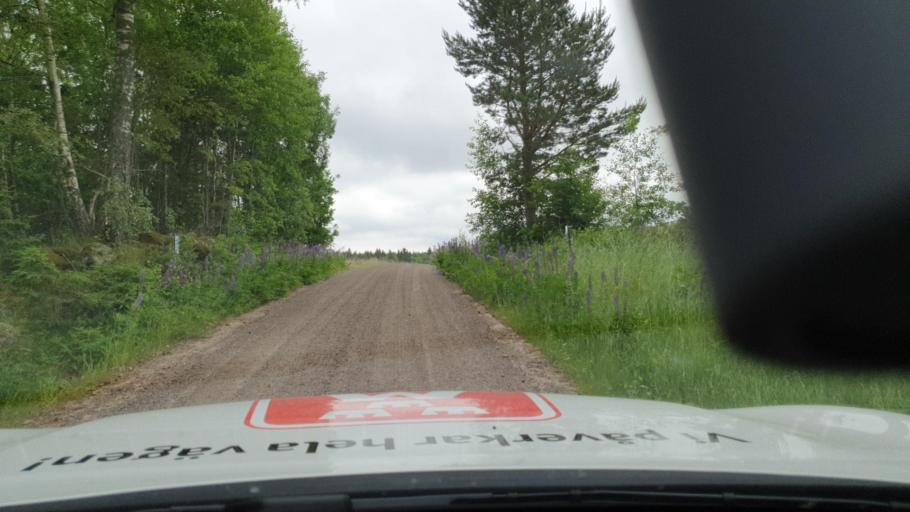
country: SE
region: Vaestra Goetaland
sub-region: Hjo Kommun
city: Hjo
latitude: 58.3947
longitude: 14.3416
